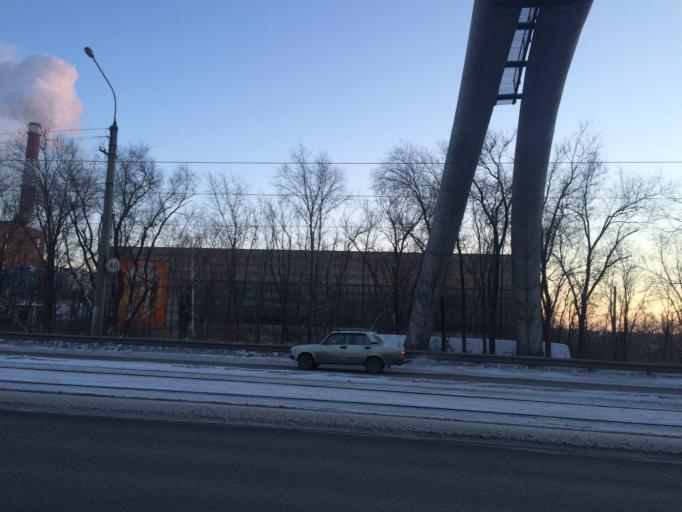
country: RU
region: Chelyabinsk
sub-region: Gorod Magnitogorsk
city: Magnitogorsk
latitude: 53.3982
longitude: 59.0149
